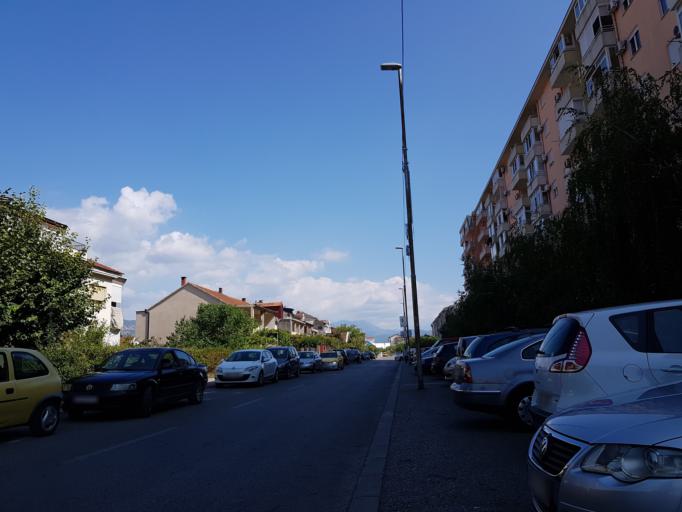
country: ME
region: Podgorica
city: Podgorica
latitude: 42.4294
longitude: 19.2730
